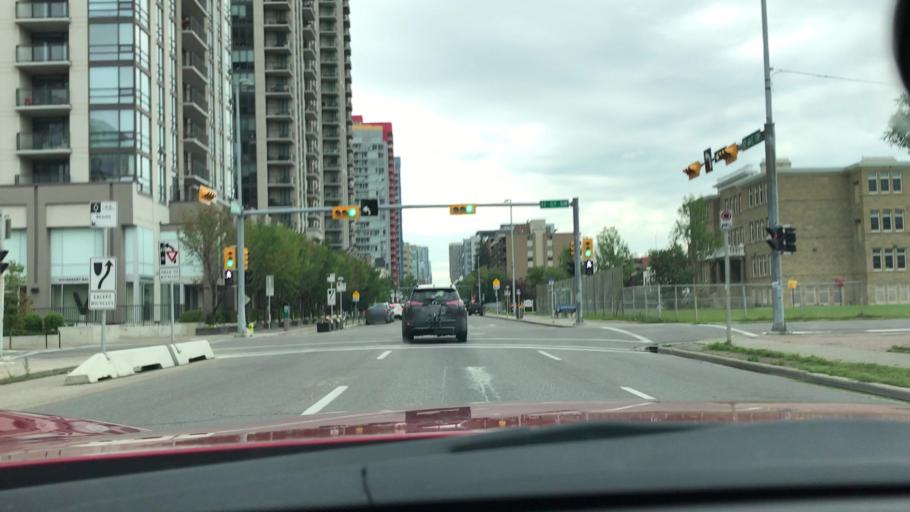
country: CA
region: Alberta
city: Calgary
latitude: 51.0422
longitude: -114.0894
